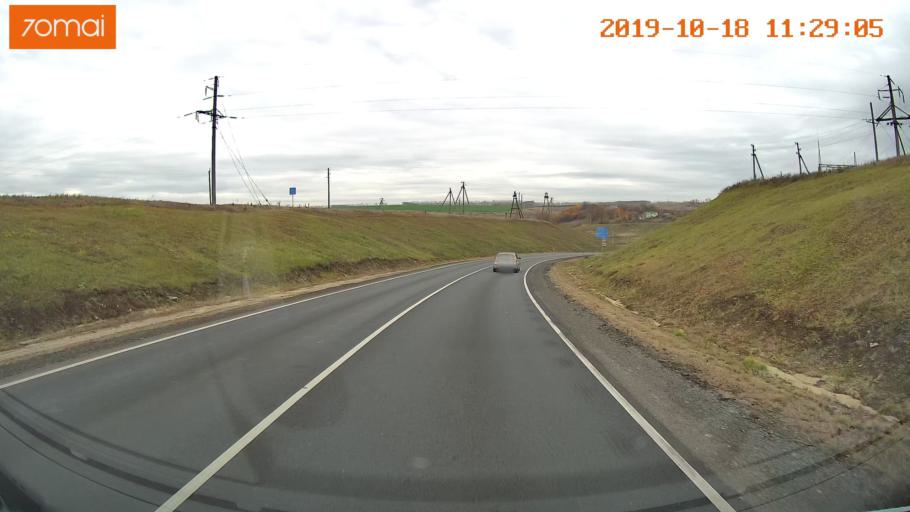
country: RU
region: Tula
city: Kimovsk
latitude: 54.1579
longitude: 38.6715
